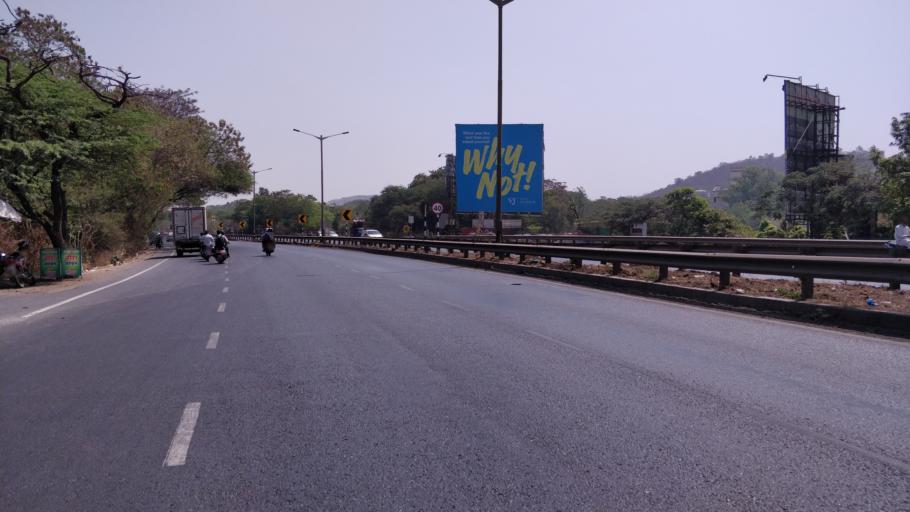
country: IN
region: Maharashtra
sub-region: Pune Division
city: Shivaji Nagar
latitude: 18.5273
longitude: 73.7760
